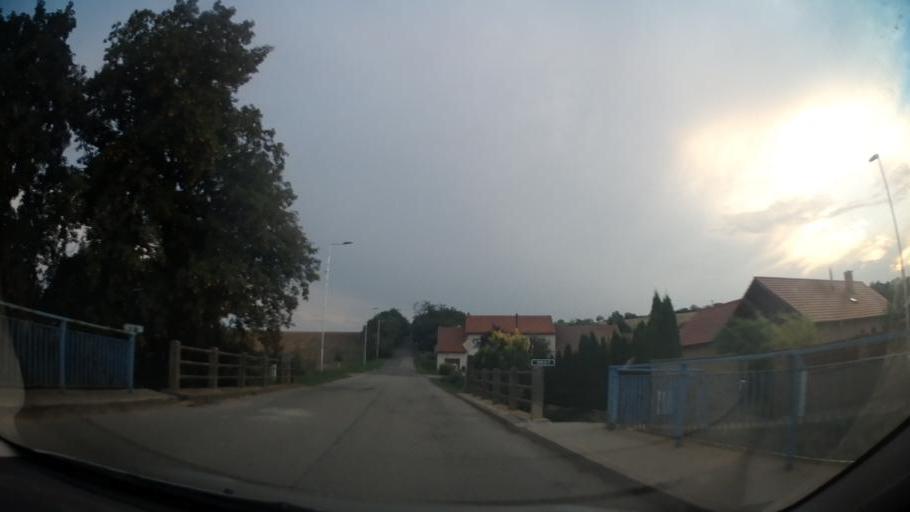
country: CZ
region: South Moravian
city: Dolni Kounice
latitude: 49.0746
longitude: 16.4924
